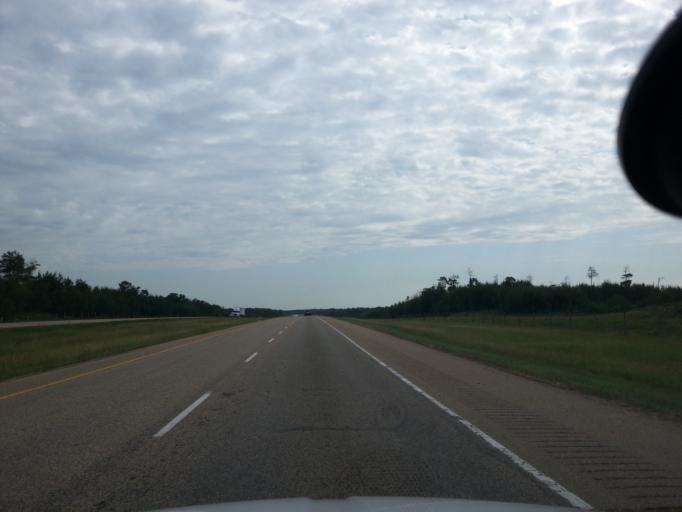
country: CA
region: Alberta
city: Lamont
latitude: 53.5690
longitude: -112.9283
